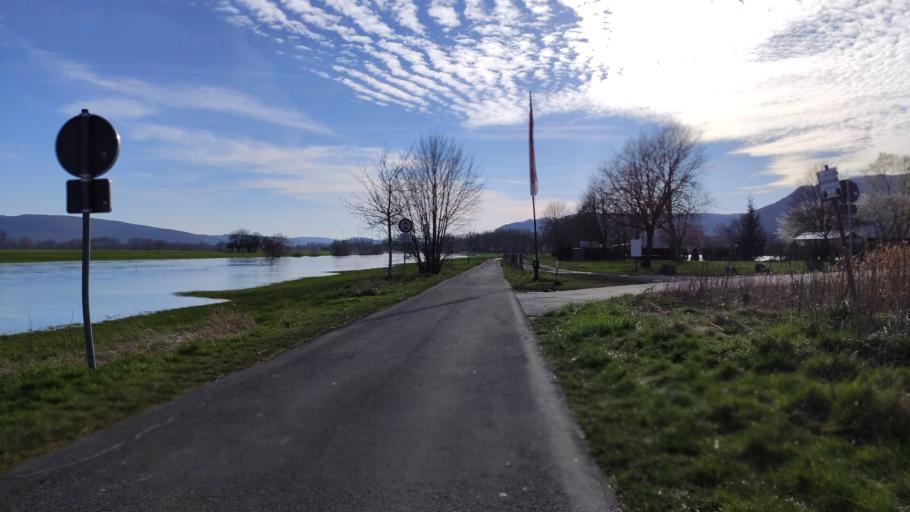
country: DE
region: Lower Saxony
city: Boffzen
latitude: 51.7494
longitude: 9.3821
